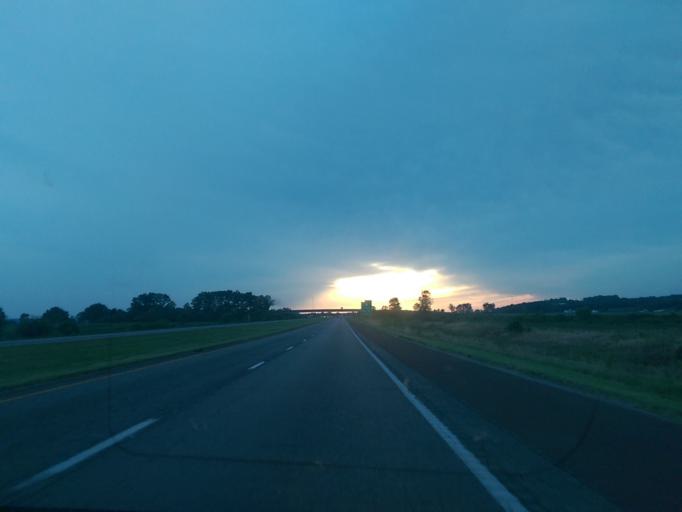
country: US
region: Missouri
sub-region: Holt County
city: Mound City
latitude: 40.1858
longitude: -95.3366
